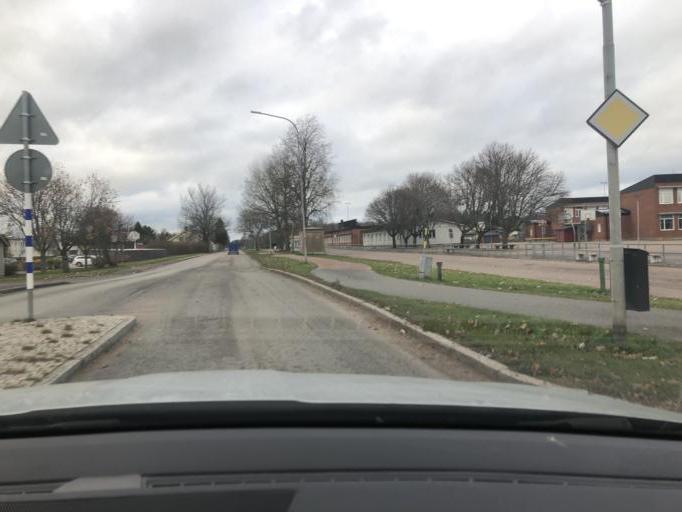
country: SE
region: Uppsala
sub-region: Tierps Kommun
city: Tierp
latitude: 60.3446
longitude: 17.5065
